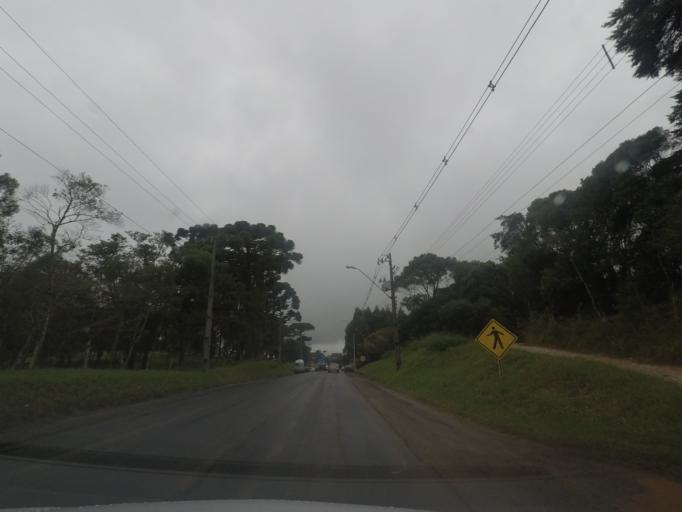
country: BR
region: Parana
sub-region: Quatro Barras
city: Quatro Barras
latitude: -25.3481
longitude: -49.0837
